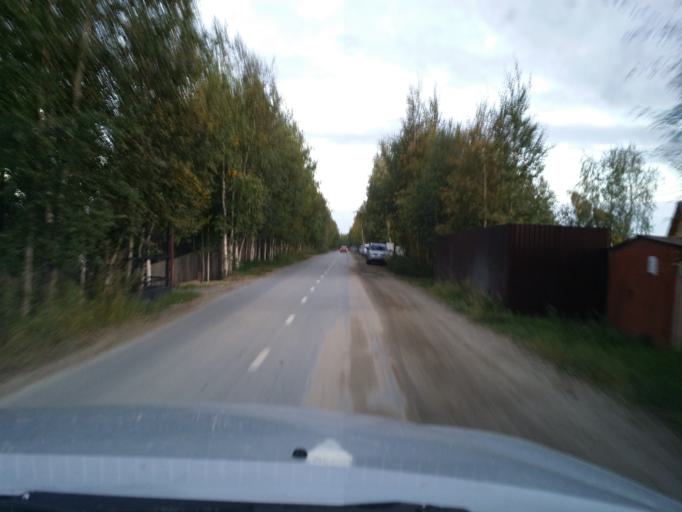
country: RU
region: Khanty-Mansiyskiy Avtonomnyy Okrug
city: Megion
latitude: 61.0796
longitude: 76.1554
